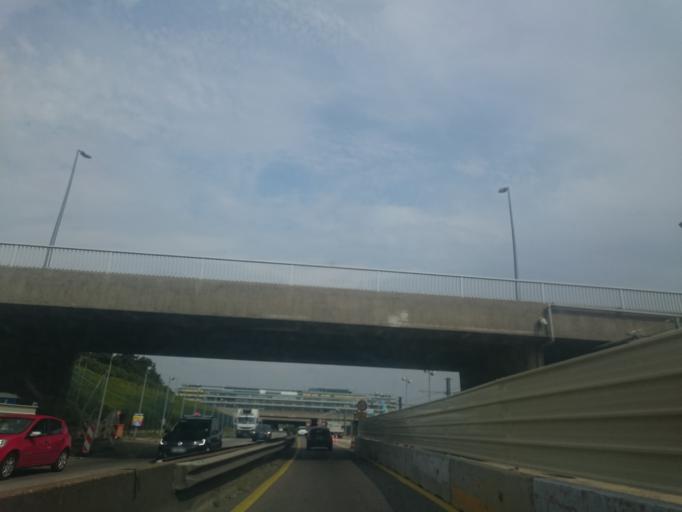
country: FR
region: Ile-de-France
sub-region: Departement de l'Essonne
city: Paray-Vieille-Poste
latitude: 48.7239
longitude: 2.3704
